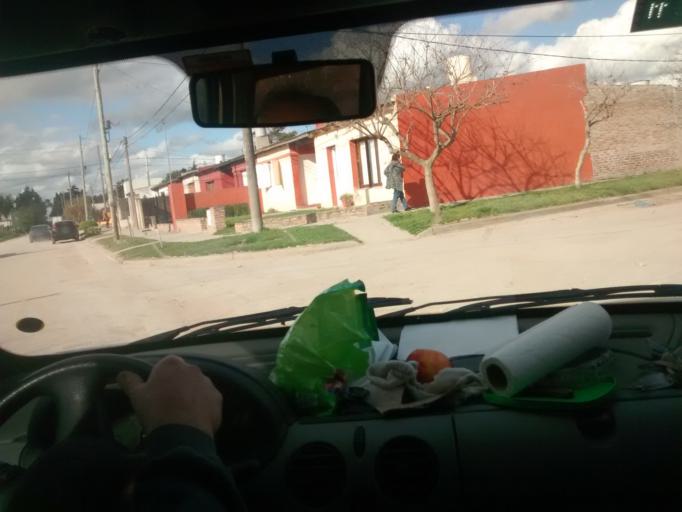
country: AR
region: Buenos Aires
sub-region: Partido de Loberia
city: Loberia
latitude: -38.1722
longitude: -58.7753
